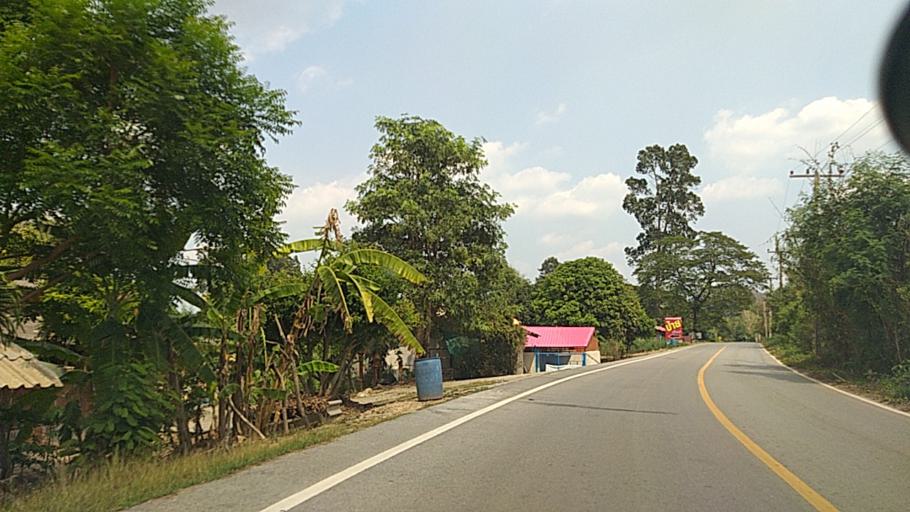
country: TH
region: Sara Buri
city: Saraburi
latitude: 14.4566
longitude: 100.9488
